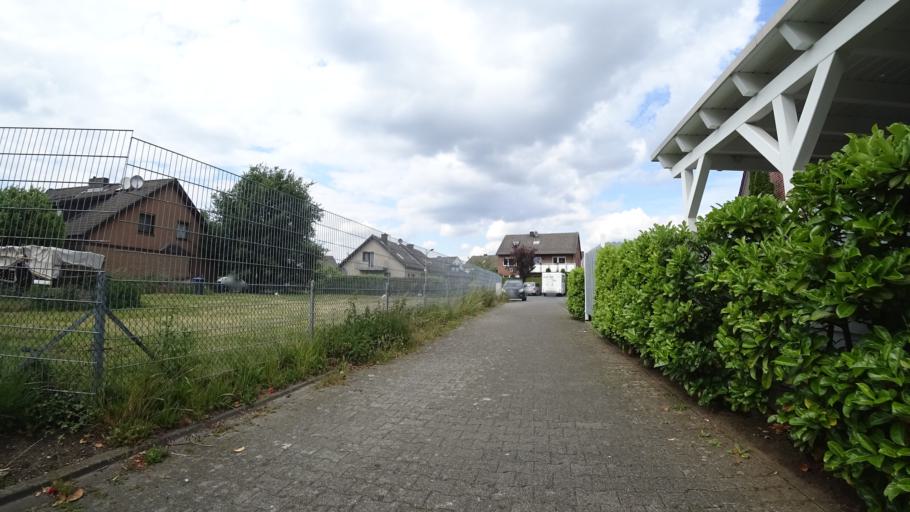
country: DE
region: North Rhine-Westphalia
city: Rietberg
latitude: 51.8154
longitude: 8.4236
